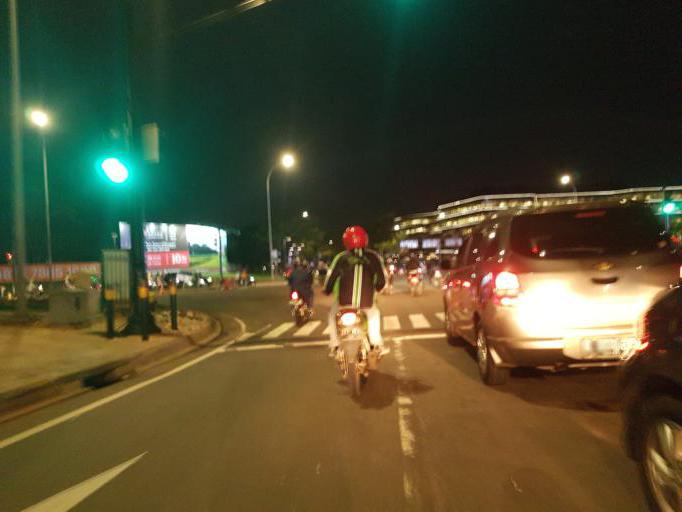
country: ID
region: West Java
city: Serpong
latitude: -6.2998
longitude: 106.6478
